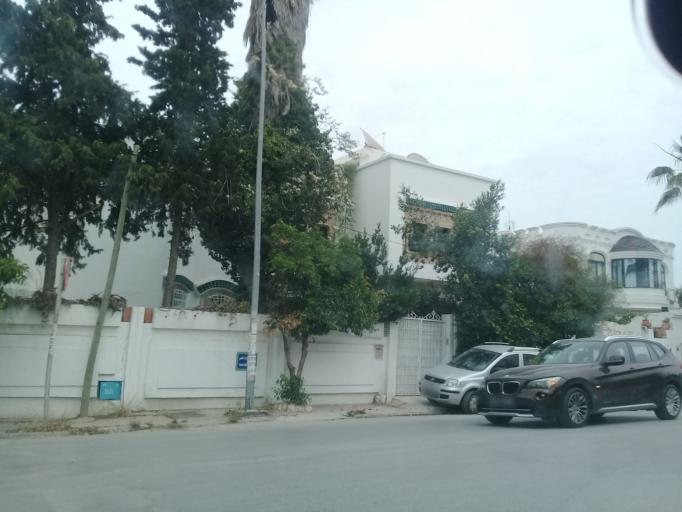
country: TN
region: Tunis
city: Tunis
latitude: 36.8453
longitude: 10.1577
